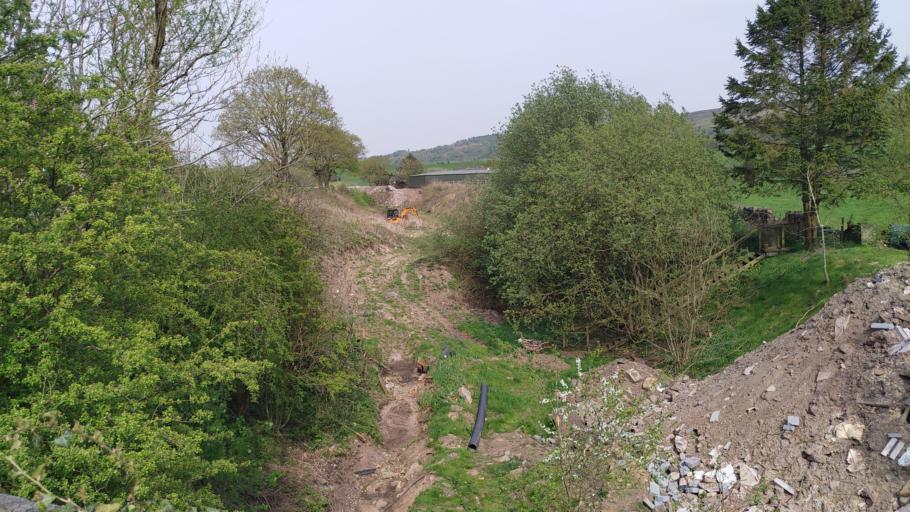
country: GB
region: England
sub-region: Lancashire
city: Chorley
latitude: 53.6721
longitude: -2.5909
